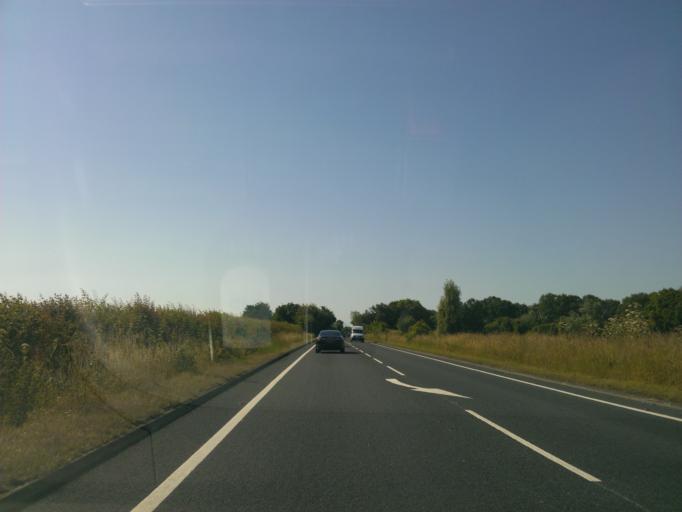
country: GB
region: England
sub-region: Essex
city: Little Clacton
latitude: 51.8319
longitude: 1.1285
